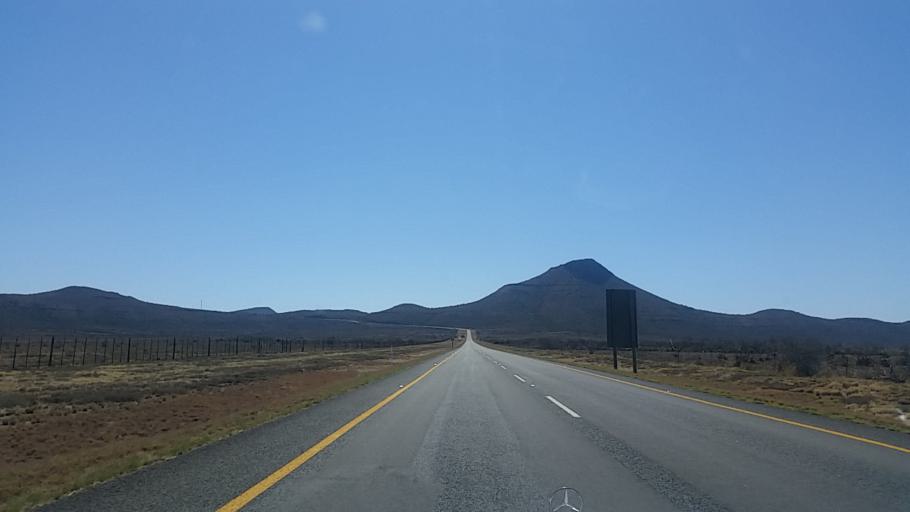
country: ZA
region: Eastern Cape
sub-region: Cacadu District Municipality
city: Graaff-Reinet
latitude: -32.1302
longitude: 24.5882
